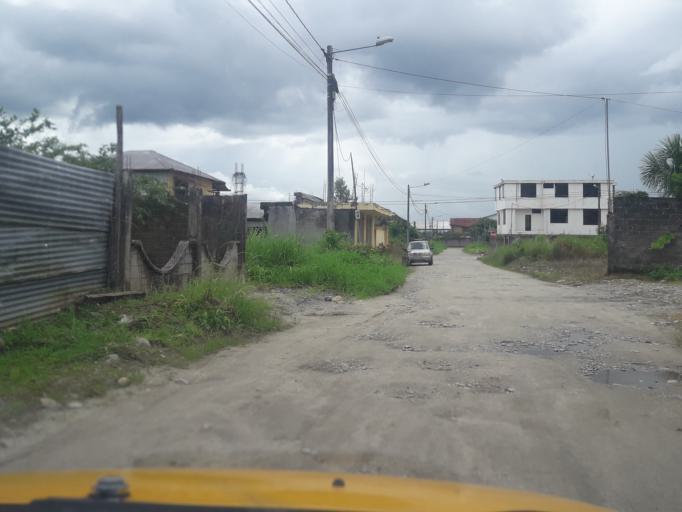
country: EC
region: Napo
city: Tena
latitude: -1.0087
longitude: -77.8151
